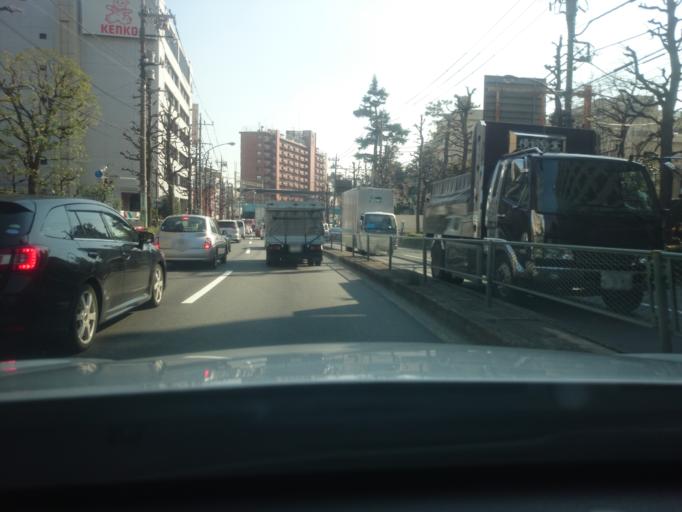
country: JP
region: Tokyo
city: Mitaka-shi
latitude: 35.6847
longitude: 139.6156
